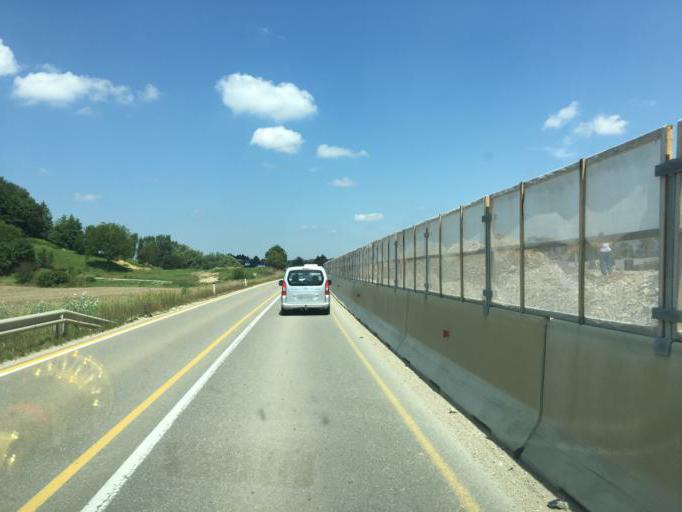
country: SI
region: Podlehnik
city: Podlehnik
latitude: 46.3509
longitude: 15.8683
